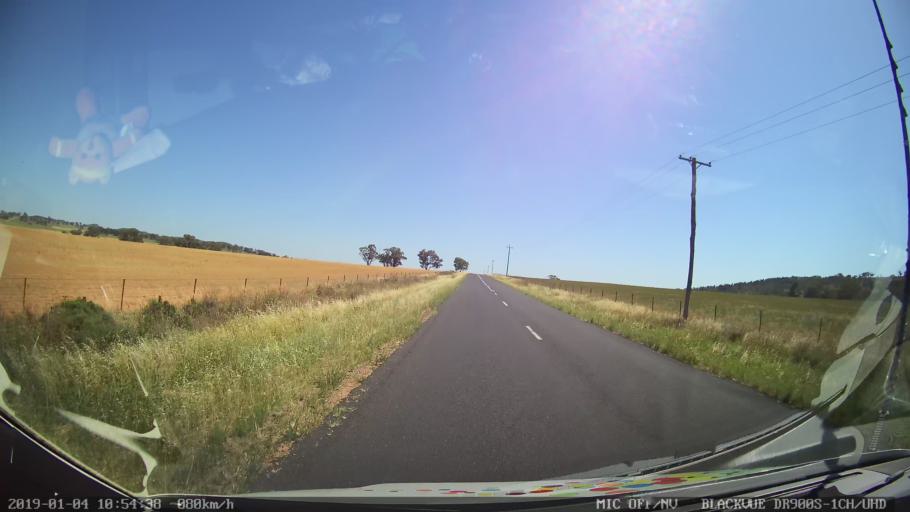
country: AU
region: New South Wales
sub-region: Cabonne
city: Molong
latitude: -33.2028
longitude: 148.6905
